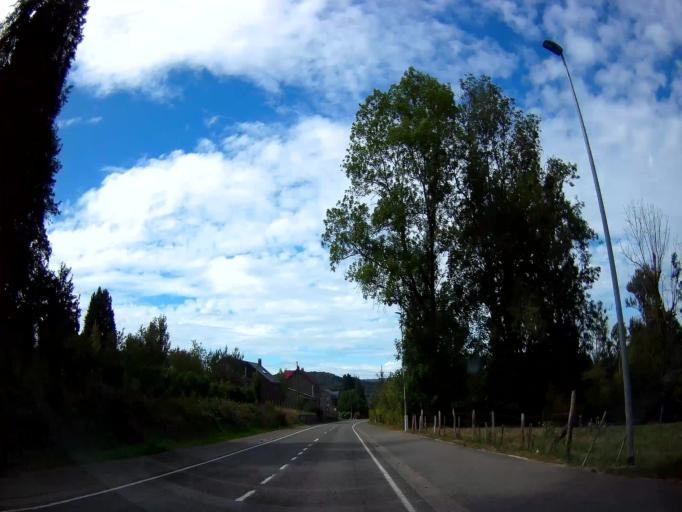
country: BE
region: Wallonia
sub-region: Province du Luxembourg
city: Rendeux
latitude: 50.2299
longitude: 5.5187
